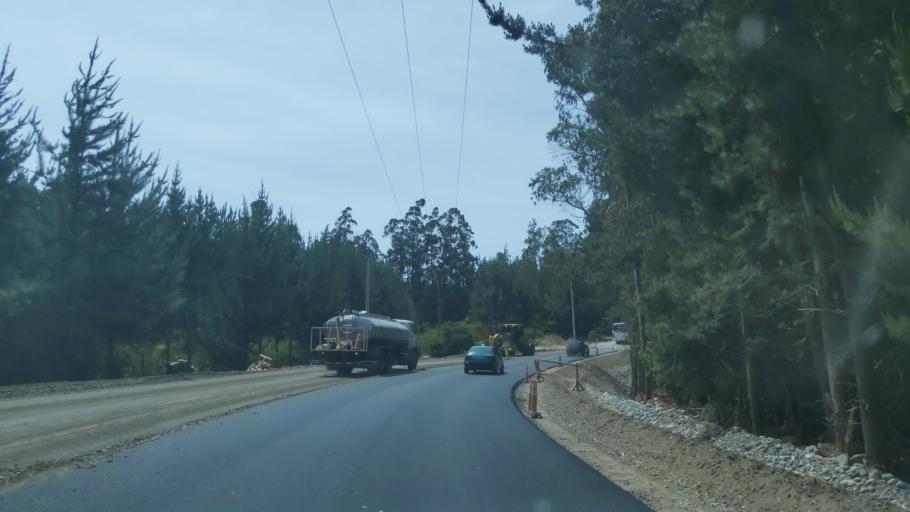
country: CL
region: Maule
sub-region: Provincia de Talca
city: Constitucion
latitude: -35.3782
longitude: -72.4218
